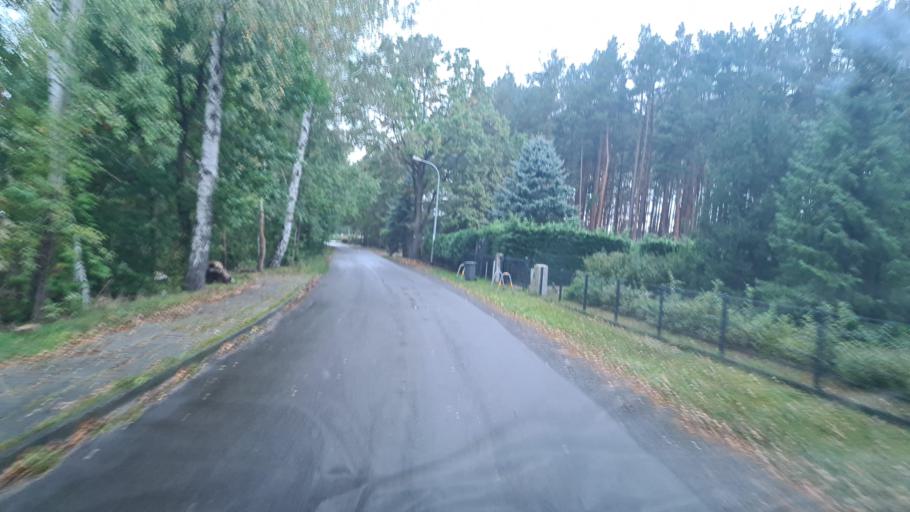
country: DE
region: Brandenburg
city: Munchehofe
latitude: 52.1260
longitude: 13.9463
